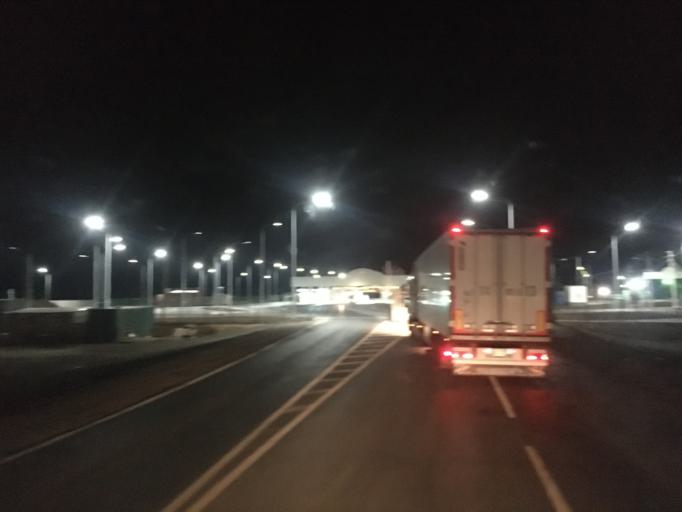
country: KZ
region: Batys Qazaqstan
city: Peremetnoe
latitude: 51.6645
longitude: 51.0060
